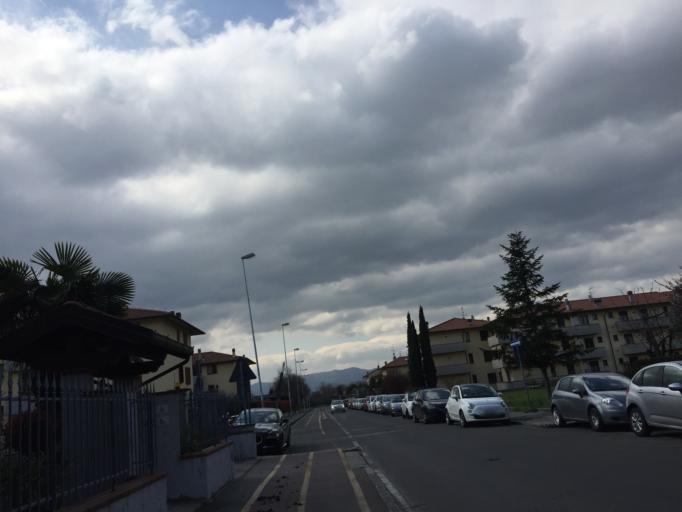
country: IT
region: Tuscany
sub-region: Provincia di Prato
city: Fornacelle
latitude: 43.8968
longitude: 11.0587
